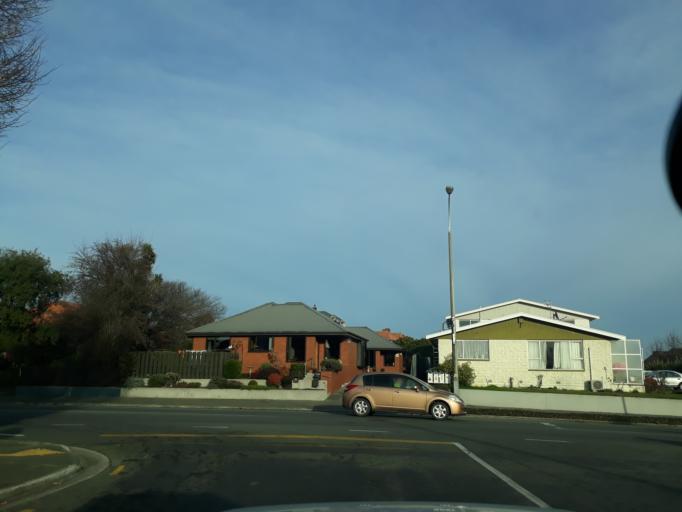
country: NZ
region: Canterbury
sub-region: Timaru District
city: Timaru
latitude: -44.3892
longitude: 171.2368
